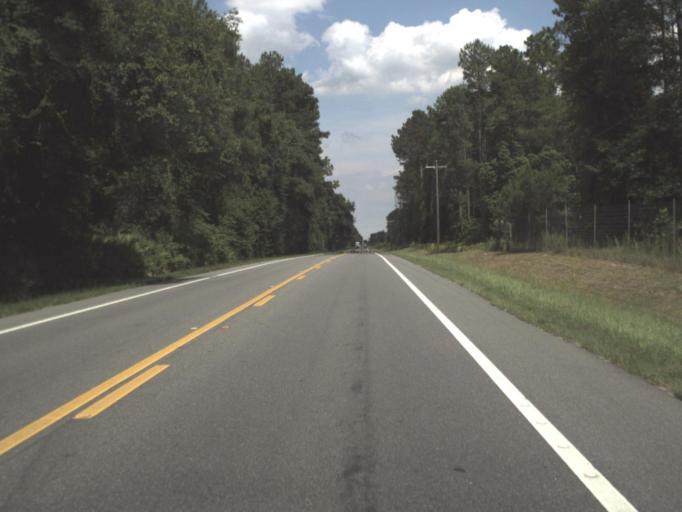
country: US
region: Florida
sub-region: Putnam County
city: Interlachen
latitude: 29.7258
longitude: -81.8411
